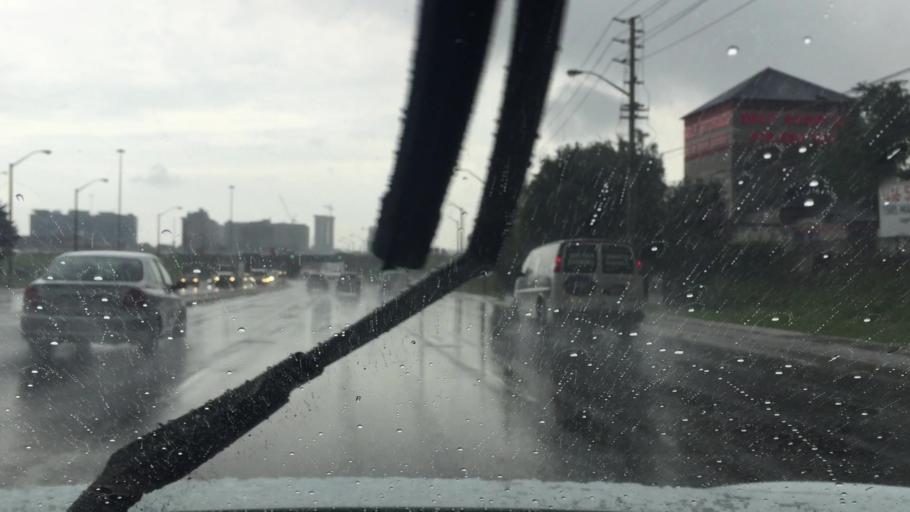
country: CA
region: Ontario
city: Scarborough
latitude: 43.7886
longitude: -79.2372
